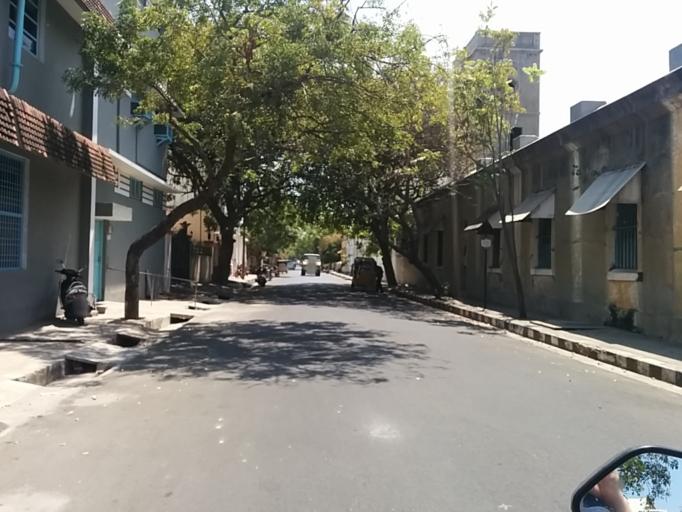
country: IN
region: Pondicherry
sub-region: Puducherry
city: Puducherry
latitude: 11.9296
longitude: 79.8346
